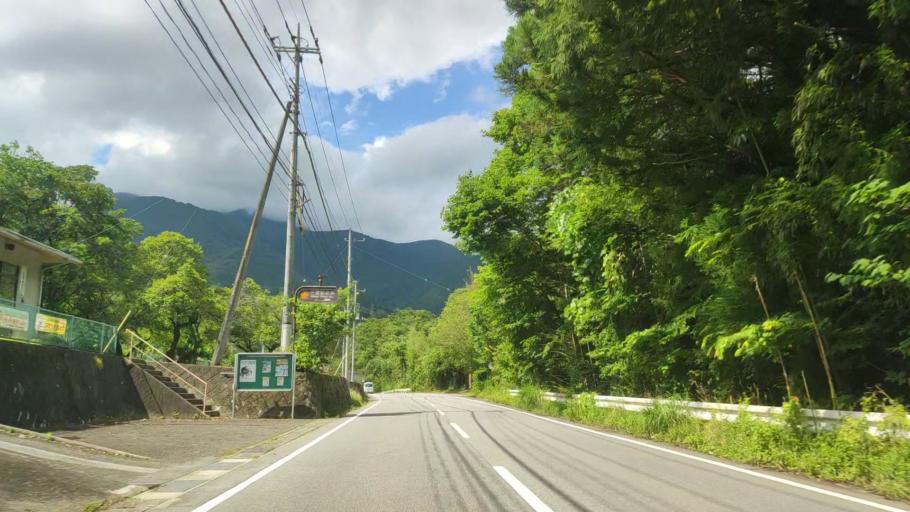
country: JP
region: Yamanashi
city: Enzan
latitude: 35.7826
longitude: 138.7391
